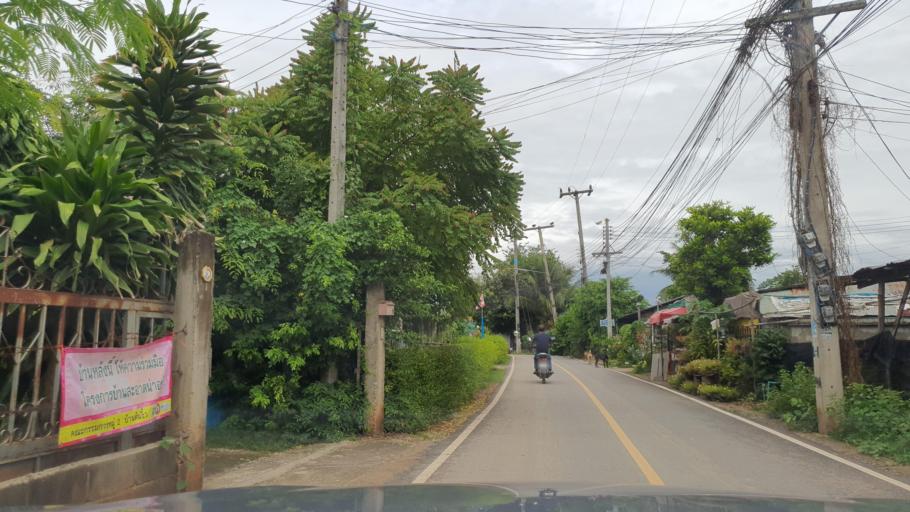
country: TH
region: Chiang Mai
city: Hang Dong
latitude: 18.7055
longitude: 98.9602
